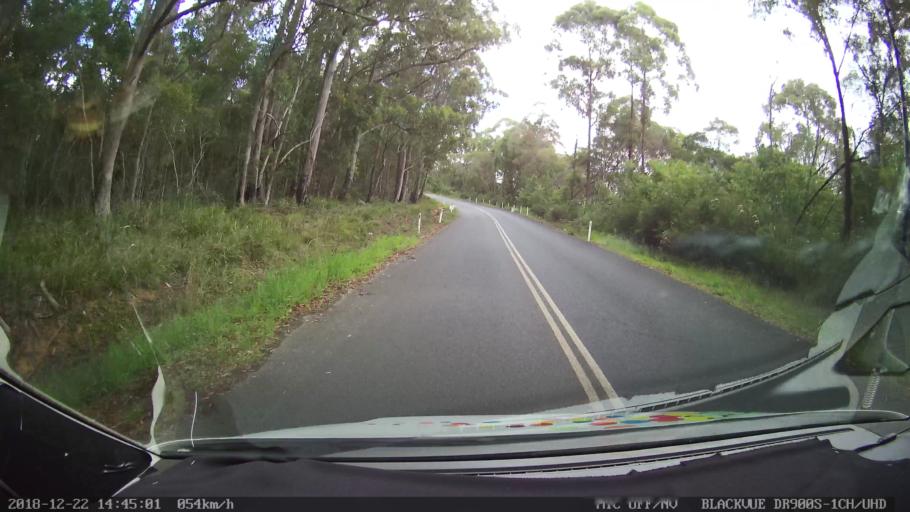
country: AU
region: New South Wales
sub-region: Bellingen
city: Dorrigo
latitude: -30.1683
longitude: 152.5723
